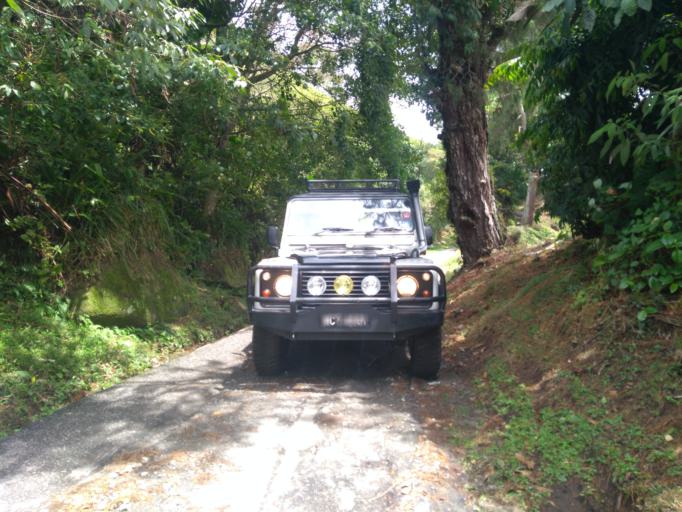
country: MY
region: Pahang
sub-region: Cameron Highlands
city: Tanah Rata
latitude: 4.5208
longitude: 101.3995
